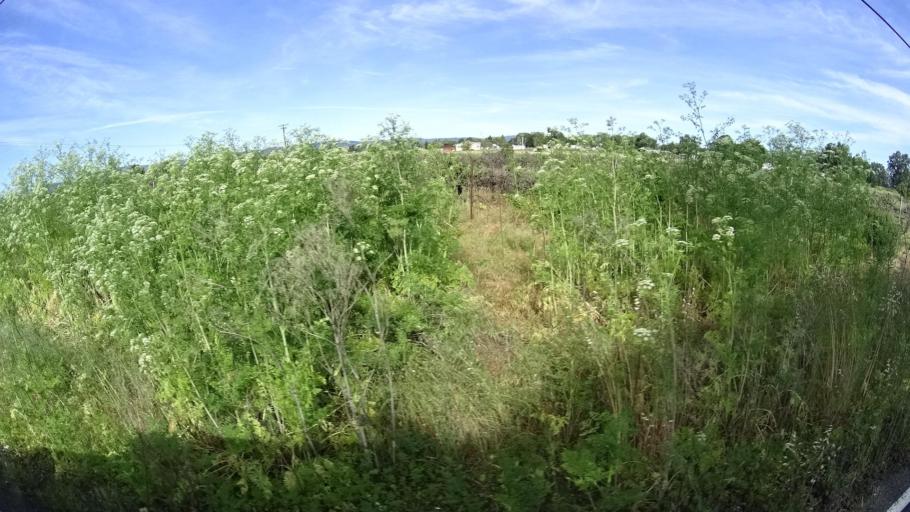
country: US
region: California
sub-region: Lake County
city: Kelseyville
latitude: 39.0096
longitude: -122.8243
